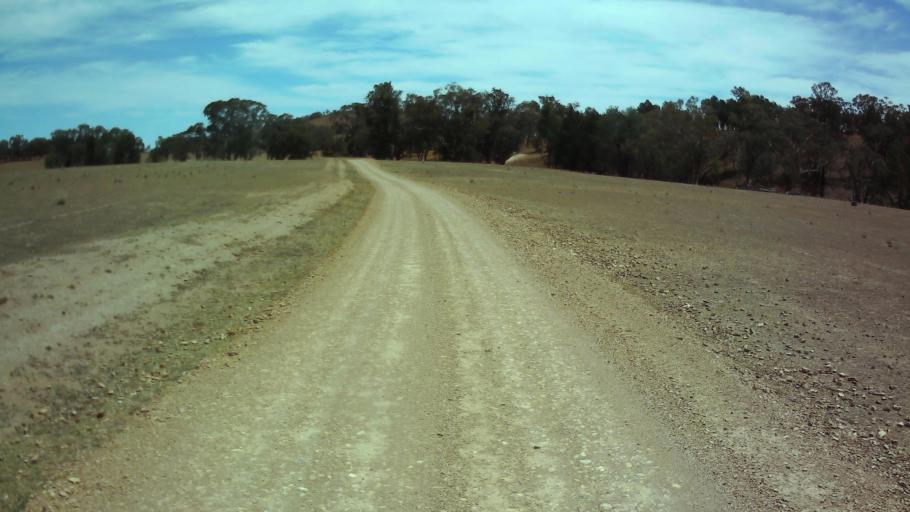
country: AU
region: New South Wales
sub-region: Weddin
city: Grenfell
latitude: -33.7426
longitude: 148.1751
